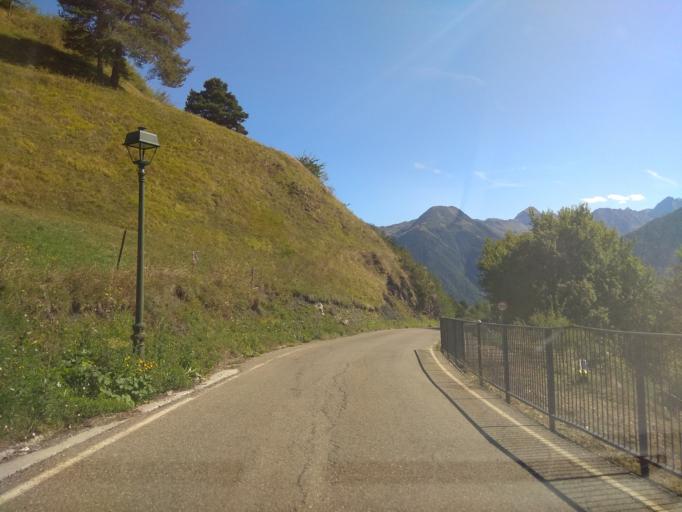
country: ES
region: Catalonia
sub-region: Provincia de Lleida
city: Les
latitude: 42.7565
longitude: 0.7133
